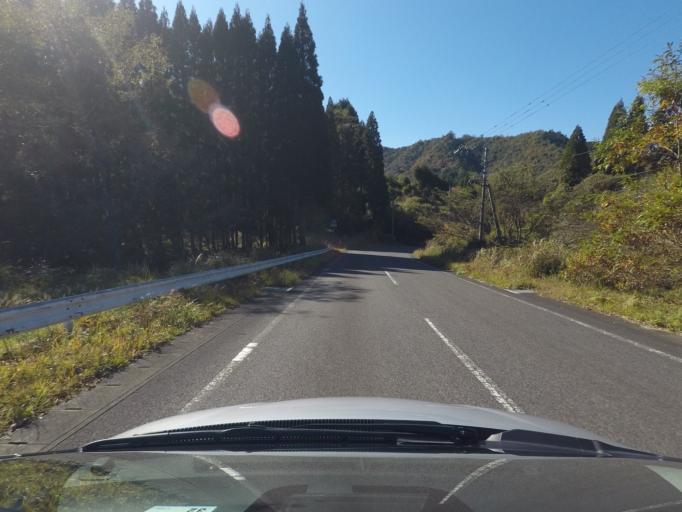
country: JP
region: Miyazaki
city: Kobayashi
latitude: 32.0565
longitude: 131.0919
